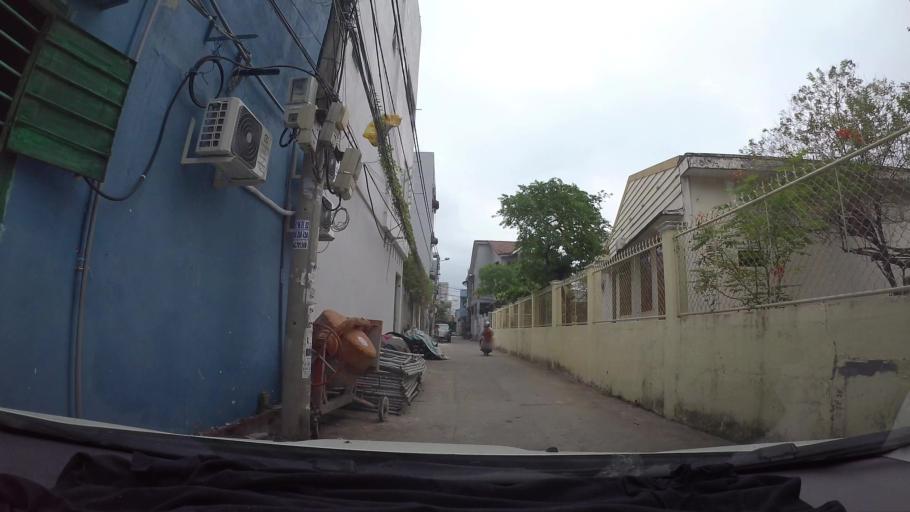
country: VN
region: Da Nang
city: Thanh Khe
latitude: 16.0720
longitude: 108.1973
